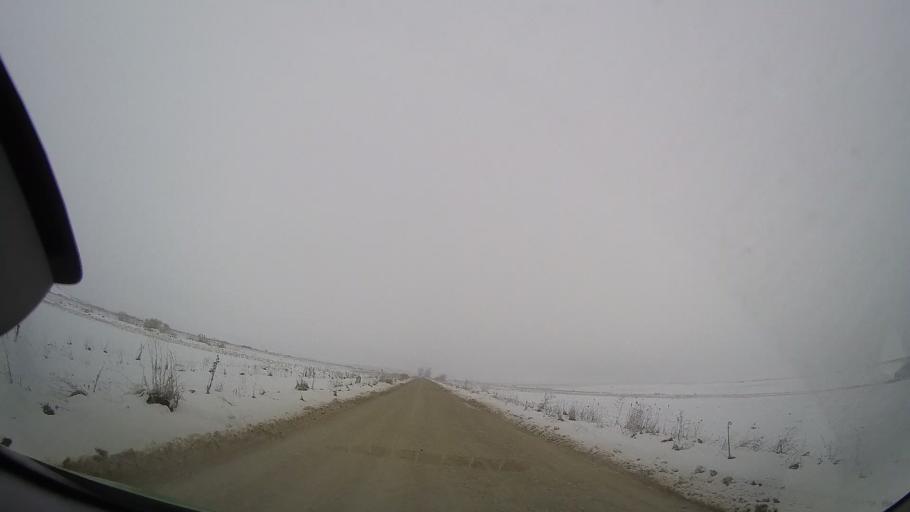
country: RO
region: Vaslui
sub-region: Comuna Todiresti
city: Todiresti
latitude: 46.8821
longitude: 27.3709
